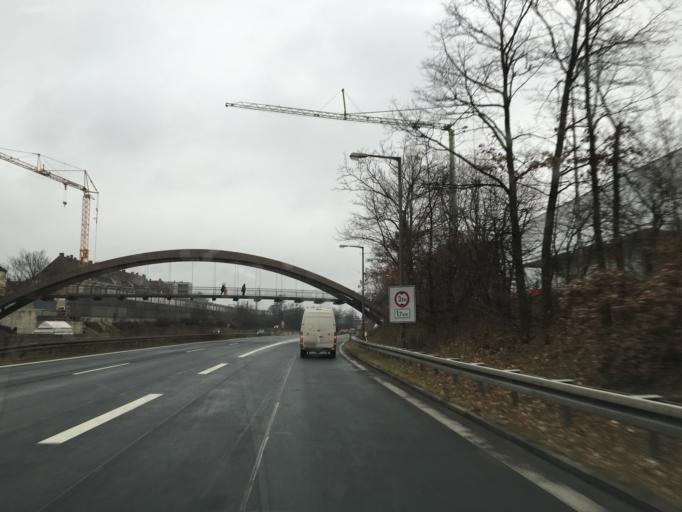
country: DE
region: Bavaria
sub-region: Regierungsbezirk Mittelfranken
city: Nuernberg
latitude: 49.4244
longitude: 11.0649
